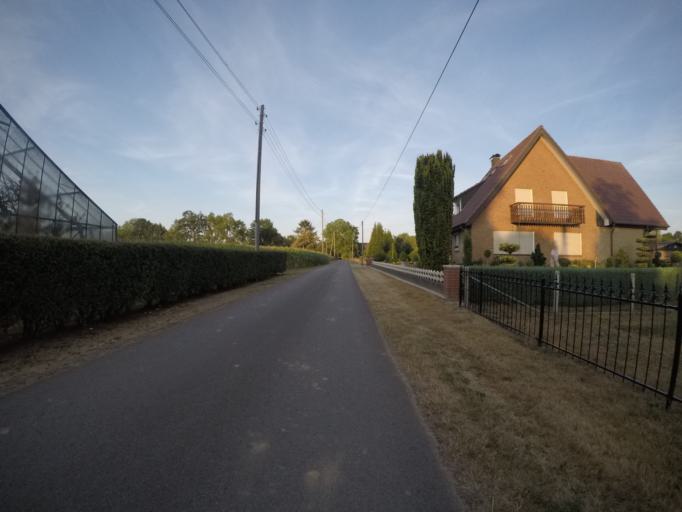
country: DE
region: North Rhine-Westphalia
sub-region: Regierungsbezirk Munster
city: Isselburg
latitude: 51.8548
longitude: 6.5177
